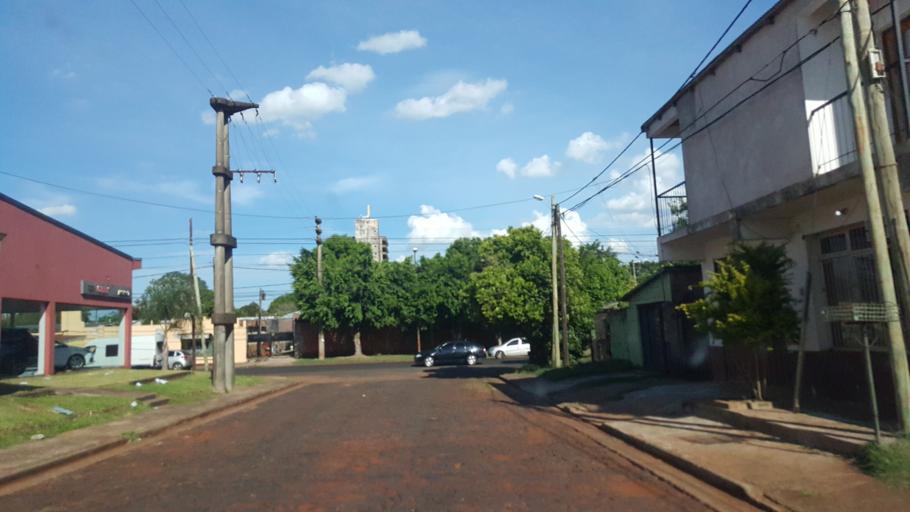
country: AR
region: Misiones
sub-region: Departamento de Capital
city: Posadas
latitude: -27.3919
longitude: -55.8979
